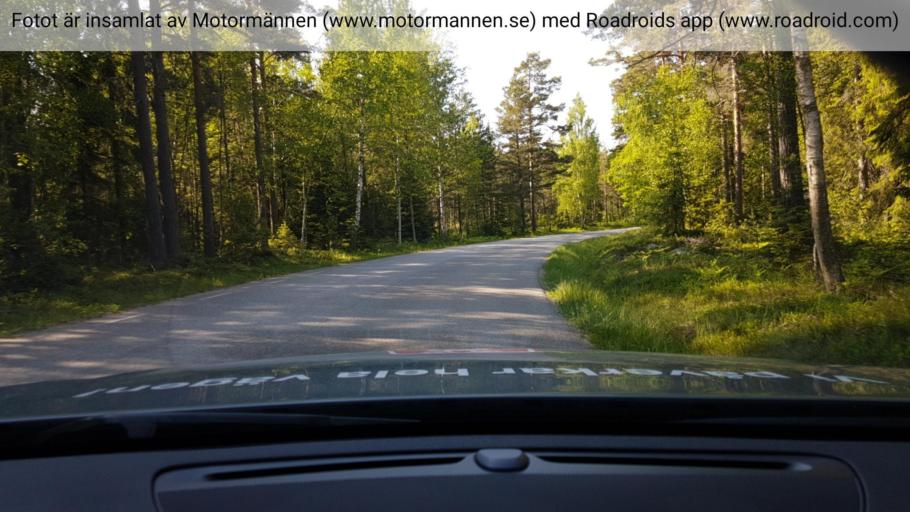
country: SE
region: Stockholm
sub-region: Varmdo Kommun
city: Mortnas
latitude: 59.2495
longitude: 18.4552
